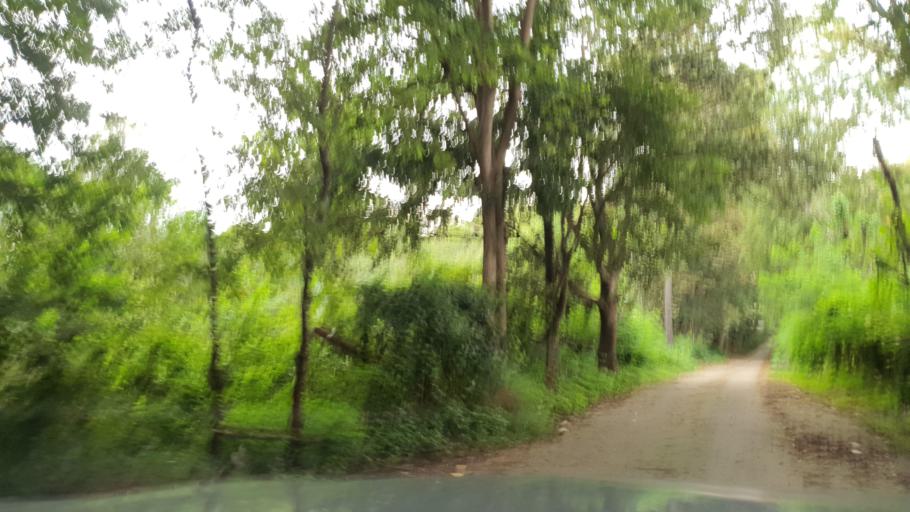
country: TH
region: Chiang Mai
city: San Sai
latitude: 18.9171
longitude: 98.9355
